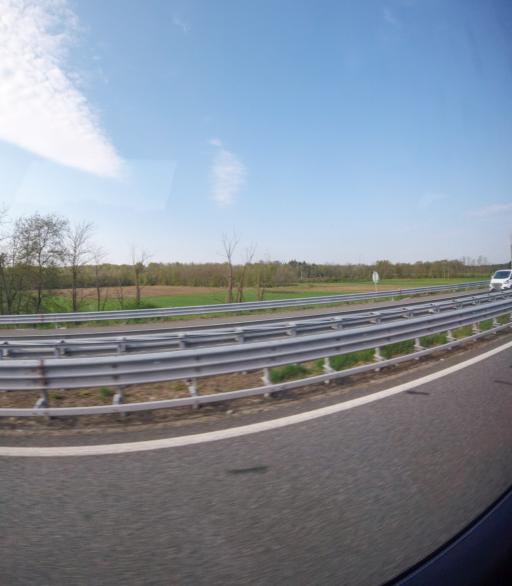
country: IT
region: Lombardy
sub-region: Provincia di Varese
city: Besnate
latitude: 45.6913
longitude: 8.7670
